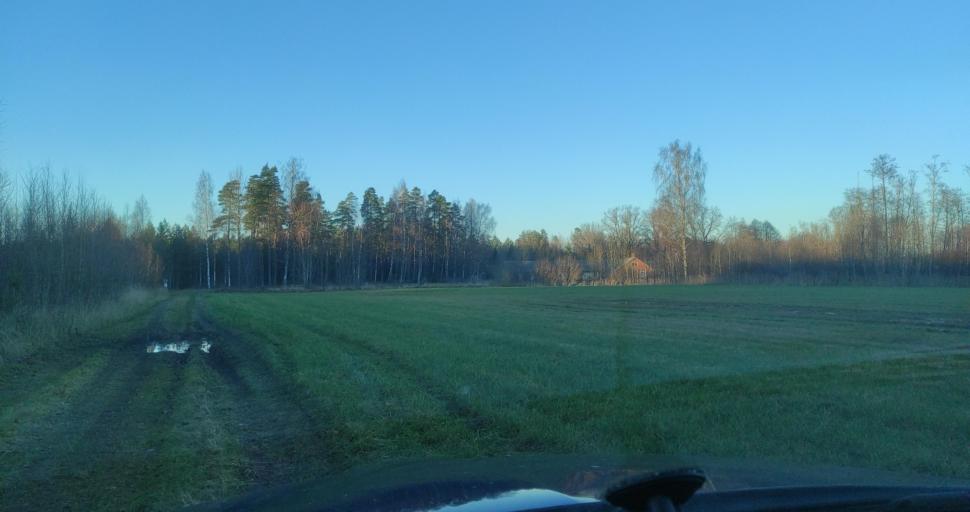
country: LV
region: Dundaga
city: Dundaga
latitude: 57.3837
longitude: 22.0853
